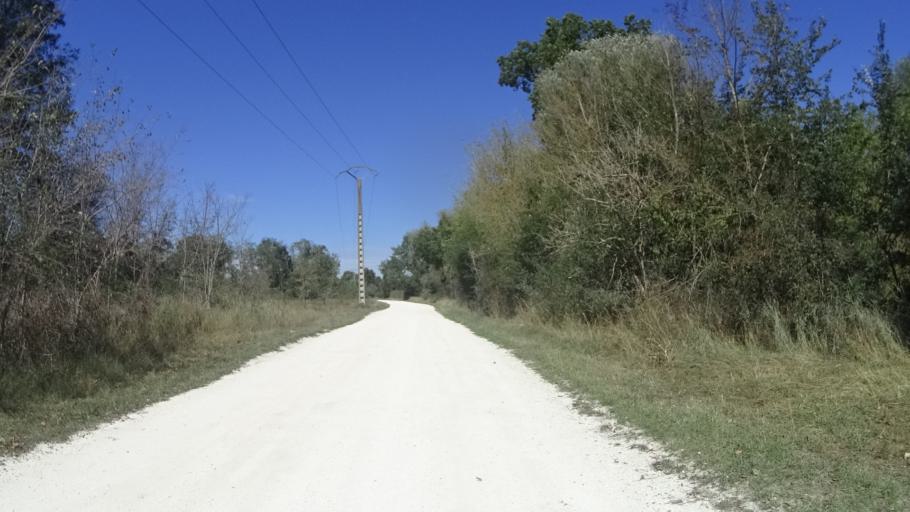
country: FR
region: Centre
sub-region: Departement du Loiret
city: Bonny-sur-Loire
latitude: 47.5392
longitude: 2.8423
